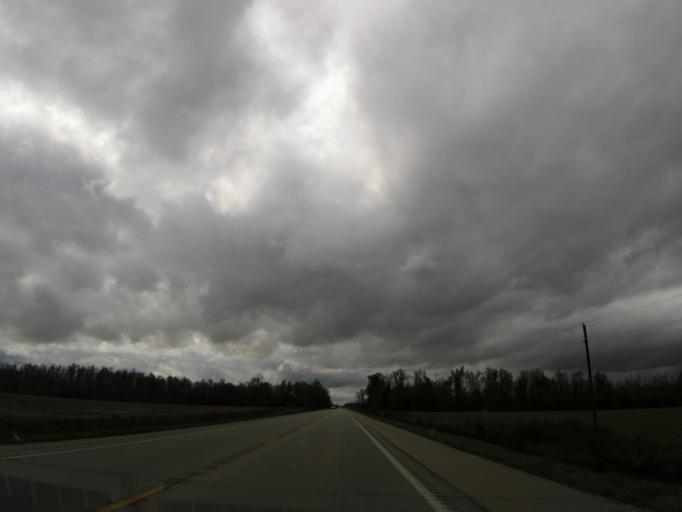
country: US
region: Missouri
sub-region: Butler County
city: Poplar Bluff
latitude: 36.6415
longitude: -90.5204
